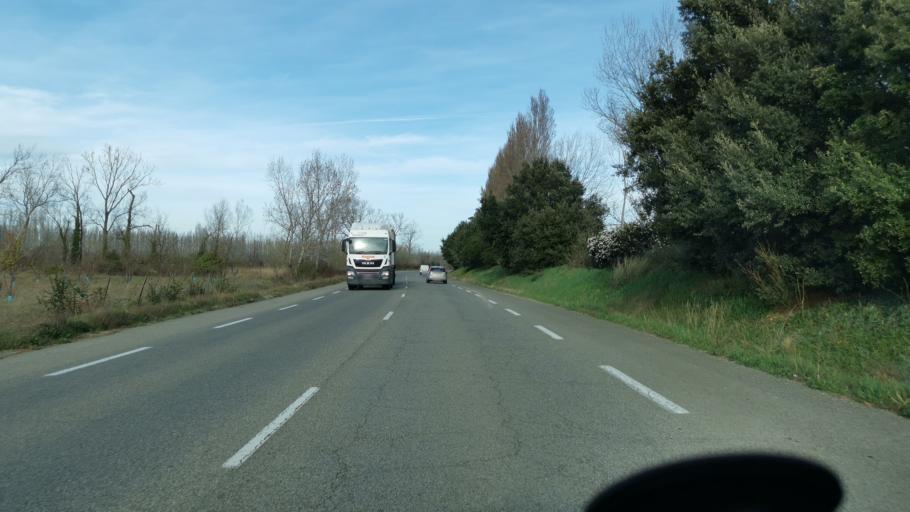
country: FR
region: Provence-Alpes-Cote d'Azur
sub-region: Departement des Bouches-du-Rhone
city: Saint-Martin-de-Crau
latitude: 43.5993
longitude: 4.7805
